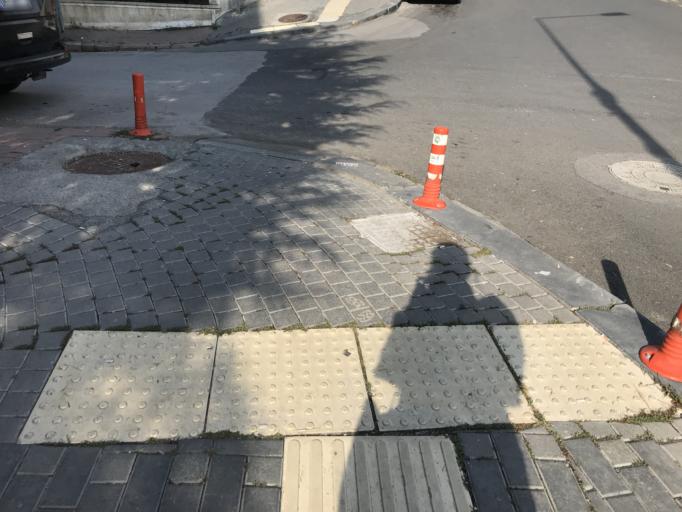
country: TR
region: Ankara
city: Ankara
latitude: 39.9174
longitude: 32.8216
